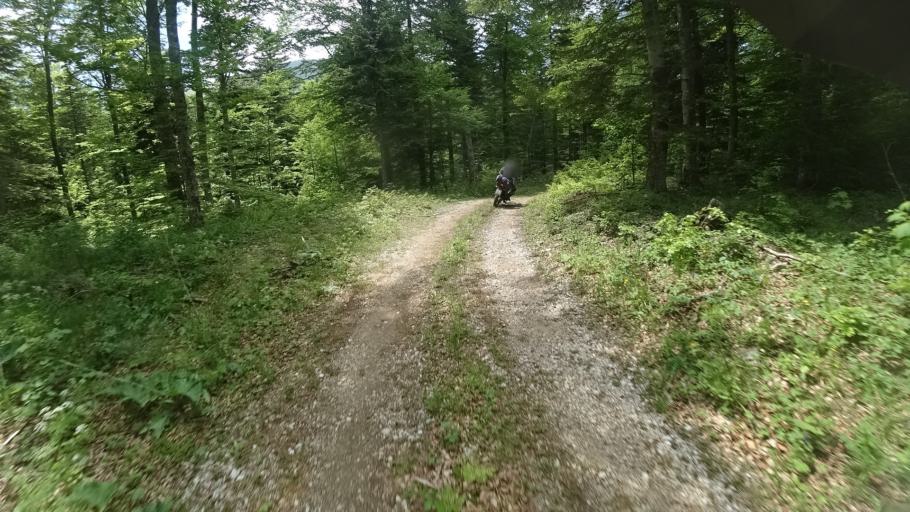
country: HR
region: Zadarska
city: Gracac
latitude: 44.4744
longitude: 15.8934
